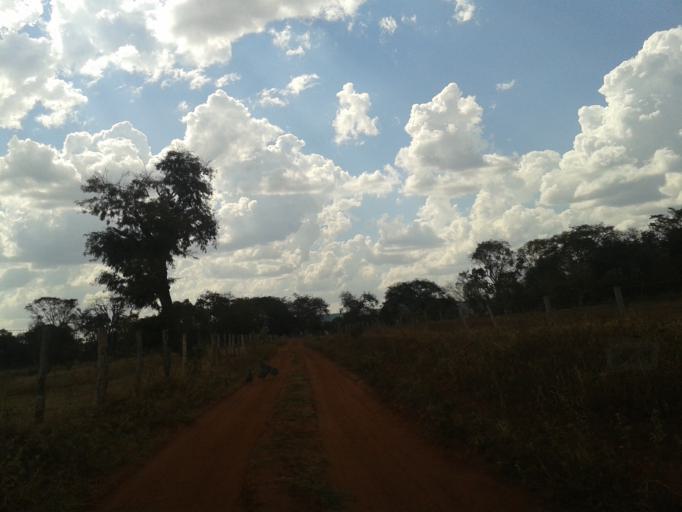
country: BR
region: Minas Gerais
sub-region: Santa Vitoria
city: Santa Vitoria
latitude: -19.1951
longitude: -49.9735
